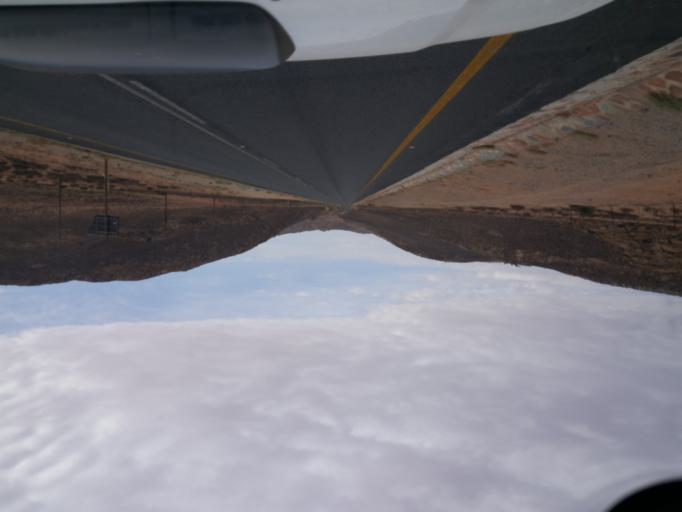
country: ZA
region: Northern Cape
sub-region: Namakwa District Municipality
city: Springbok
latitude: -29.4589
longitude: 17.8384
